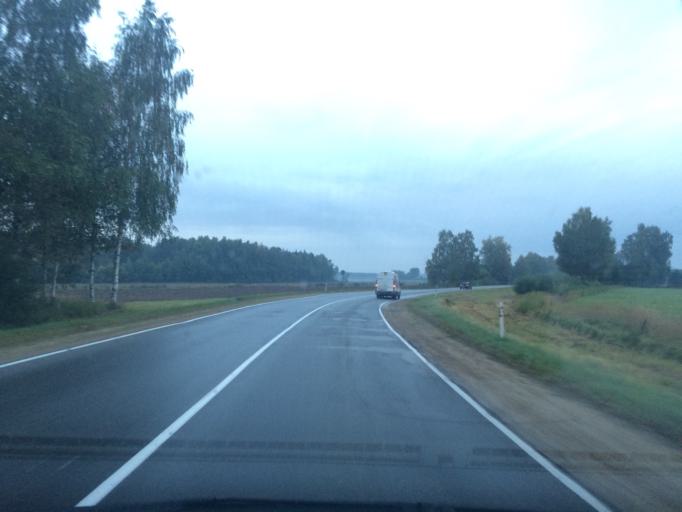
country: LV
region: Salas
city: Sala
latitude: 56.5495
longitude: 25.7985
